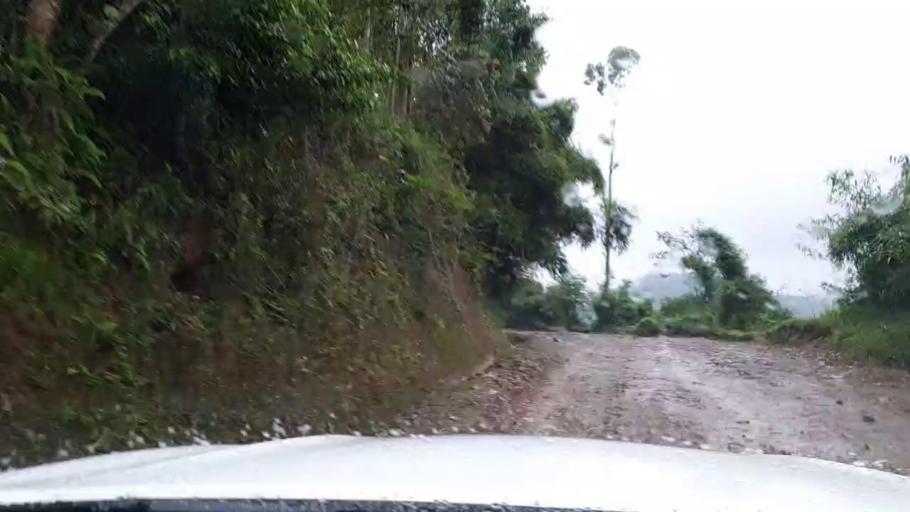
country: RW
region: Western Province
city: Cyangugu
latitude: -2.4632
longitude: 29.0335
